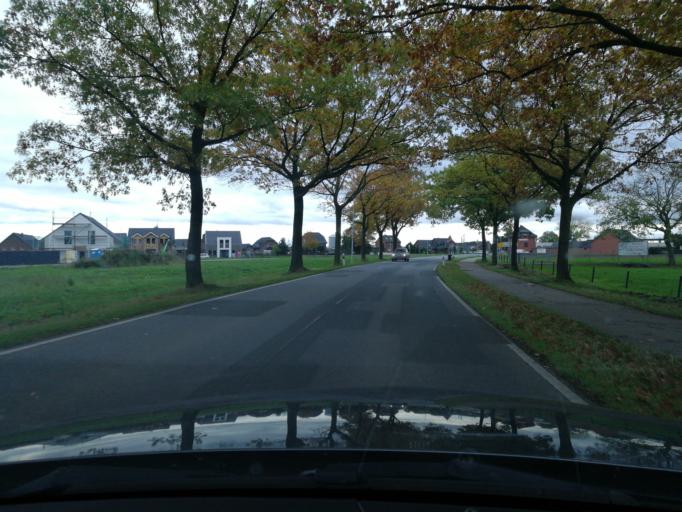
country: DE
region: North Rhine-Westphalia
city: Straelen
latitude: 51.4641
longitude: 6.2414
